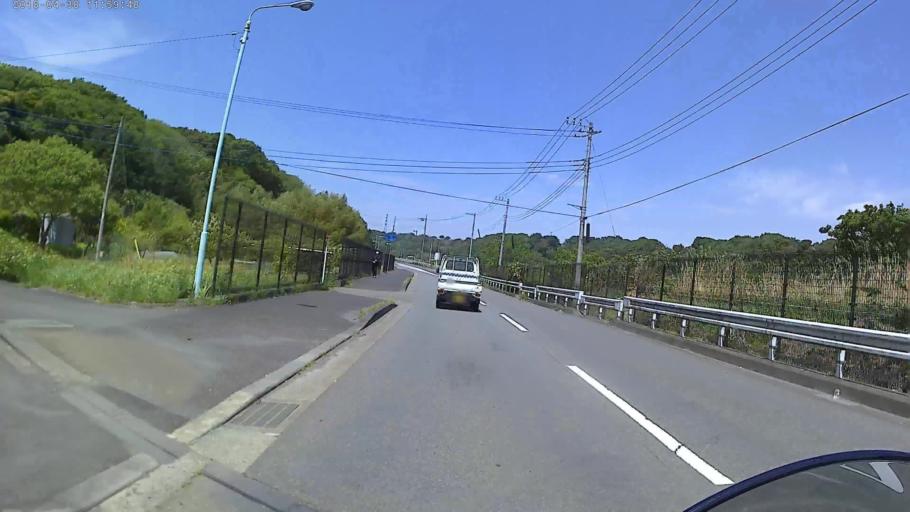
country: JP
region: Kanagawa
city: Zama
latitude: 35.5101
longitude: 139.3287
